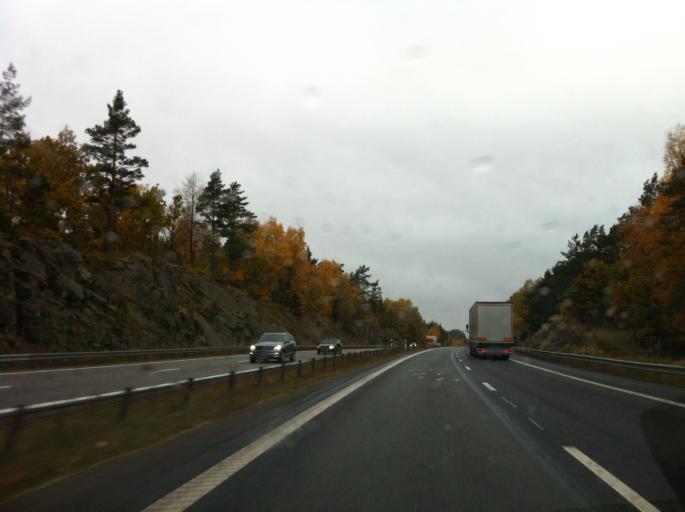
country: SE
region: Joenkoeping
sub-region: Jonkopings Kommun
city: Graenna
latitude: 57.9785
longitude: 14.3938
